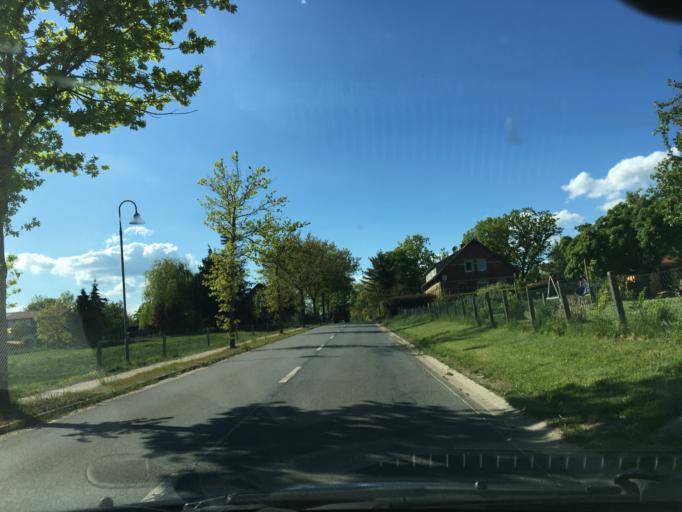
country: DE
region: Lower Saxony
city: Gartow
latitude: 53.0554
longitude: 11.4306
